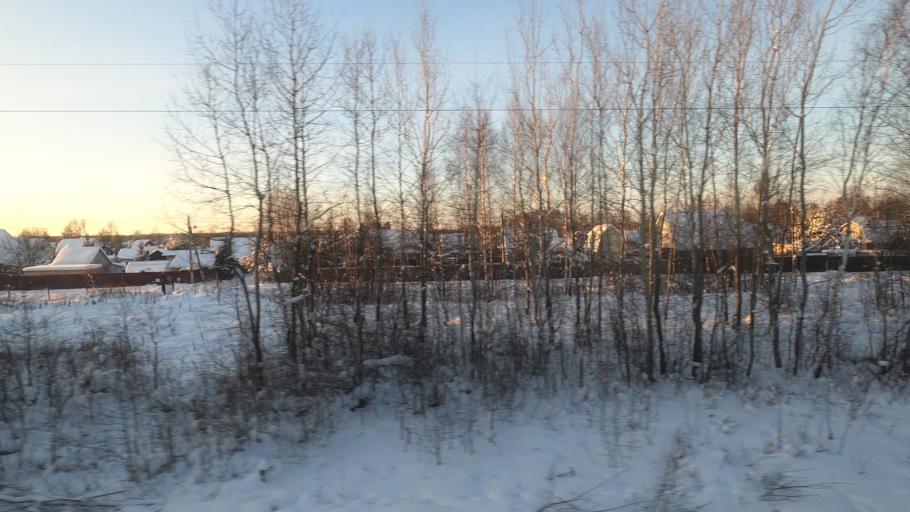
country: RU
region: Moskovskaya
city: Orud'yevo
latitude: 56.4372
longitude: 37.5075
